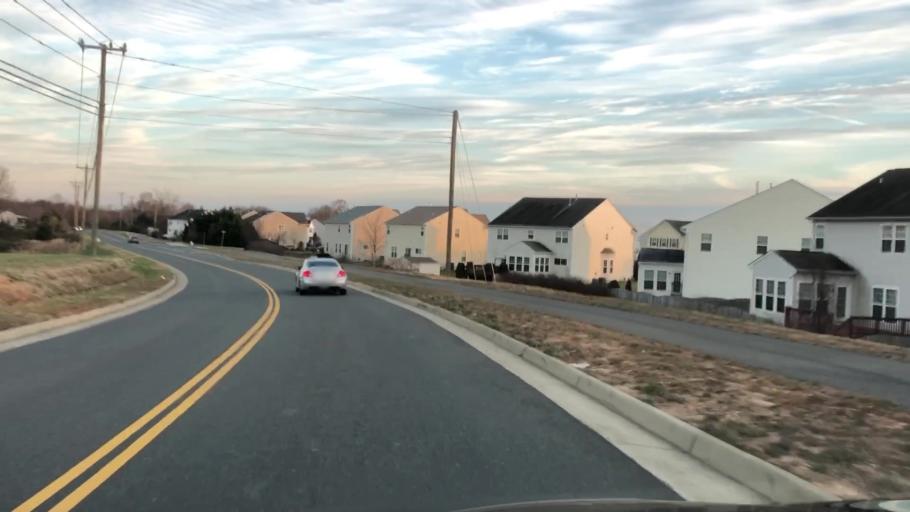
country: US
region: Virginia
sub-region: Stafford County
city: Falmouth
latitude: 38.3718
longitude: -77.5015
